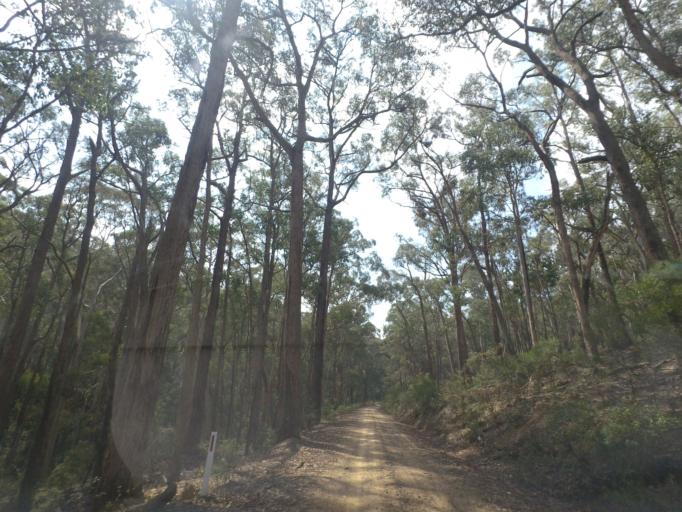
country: AU
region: Victoria
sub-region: Moorabool
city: Bacchus Marsh
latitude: -37.4622
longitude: 144.3652
